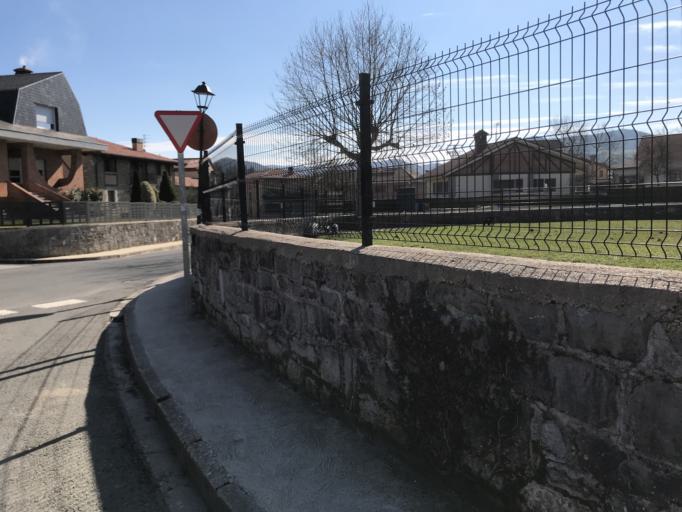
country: ES
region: Basque Country
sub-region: Provincia de Alava
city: Gasteiz / Vitoria
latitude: 42.8187
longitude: -2.6529
